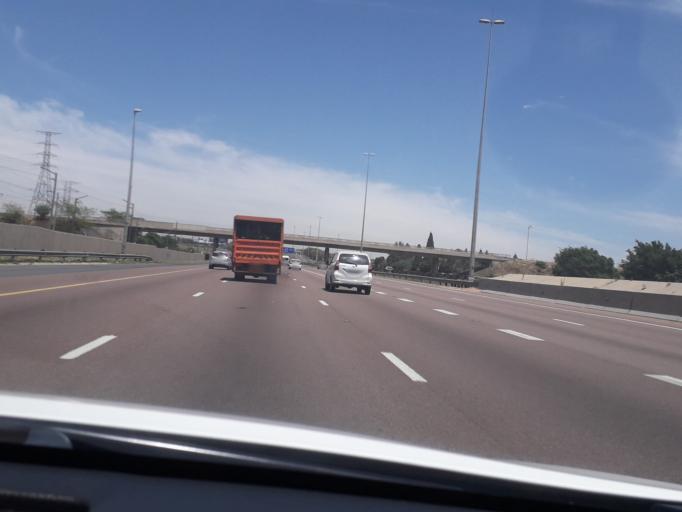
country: ZA
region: Gauteng
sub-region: City of Tshwane Metropolitan Municipality
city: Centurion
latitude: -25.8734
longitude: 28.1792
